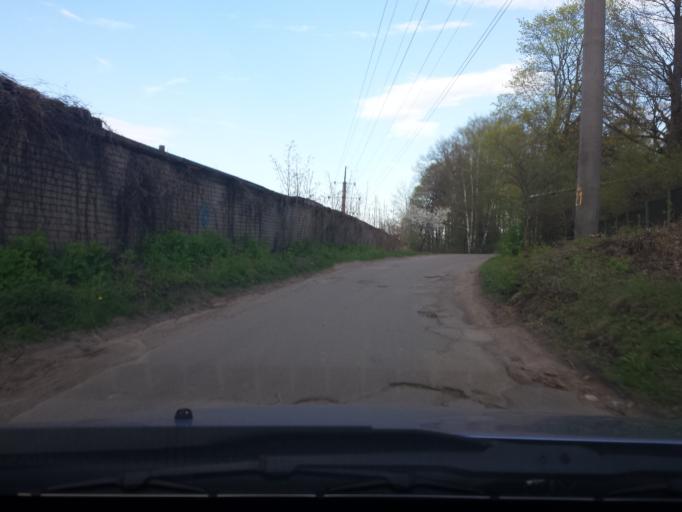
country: LV
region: Riga
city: Jaunciems
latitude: 56.9963
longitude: 24.2204
